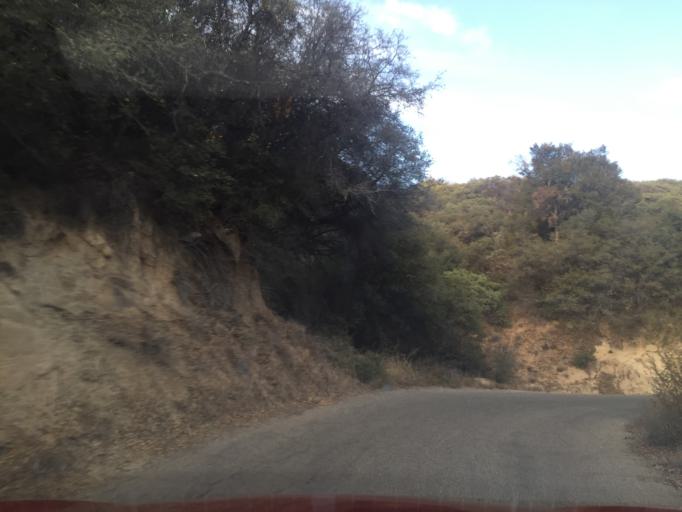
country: US
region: California
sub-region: Tulare County
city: Three Rivers
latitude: 36.4346
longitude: -118.7388
